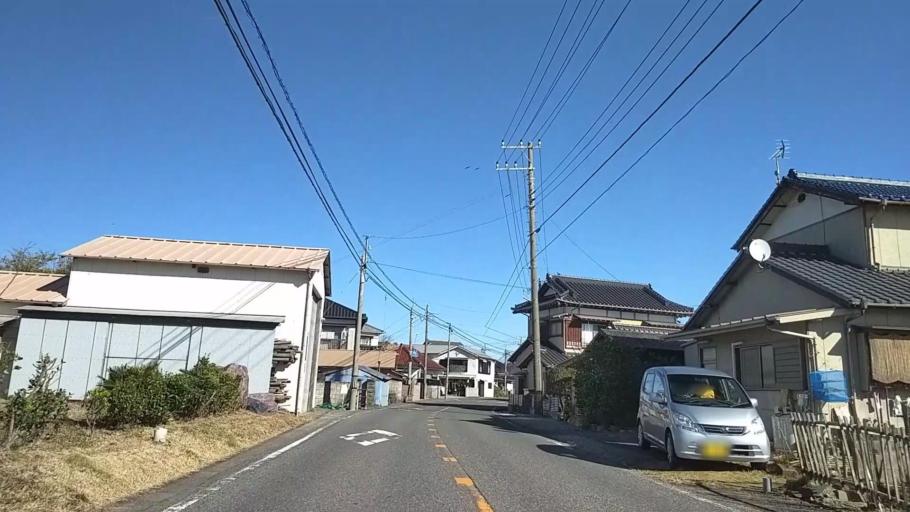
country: JP
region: Chiba
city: Tateyama
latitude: 34.9452
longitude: 139.9614
